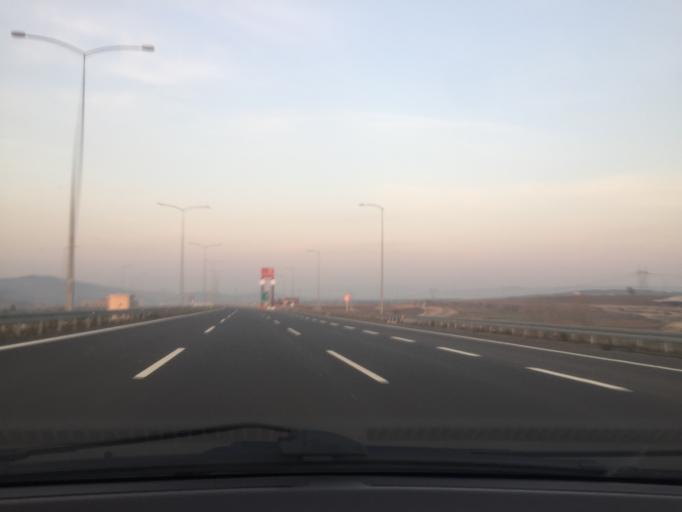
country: TR
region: Bursa
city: Mahmudiye
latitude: 40.2721
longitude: 28.6078
